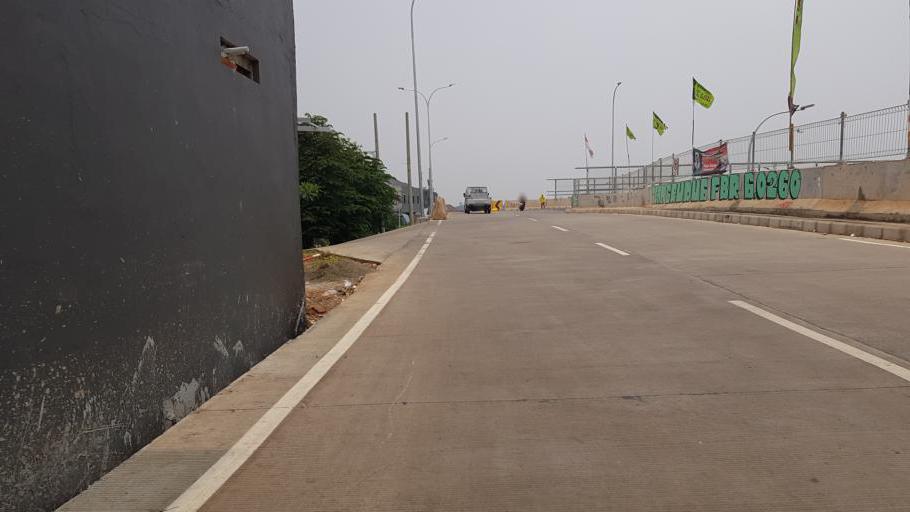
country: ID
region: West Java
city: Pamulang
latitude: -6.3311
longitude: 106.8005
